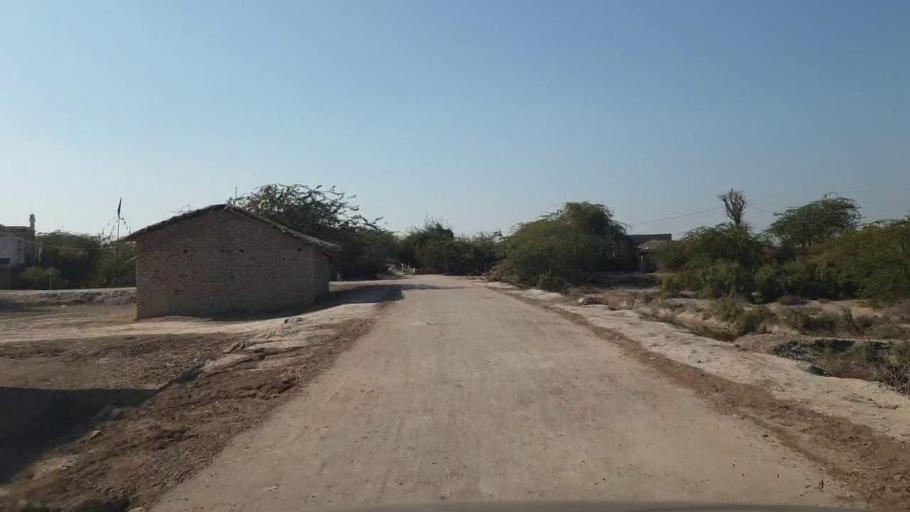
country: PK
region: Sindh
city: Shahpur Chakar
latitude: 26.1585
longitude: 68.6760
